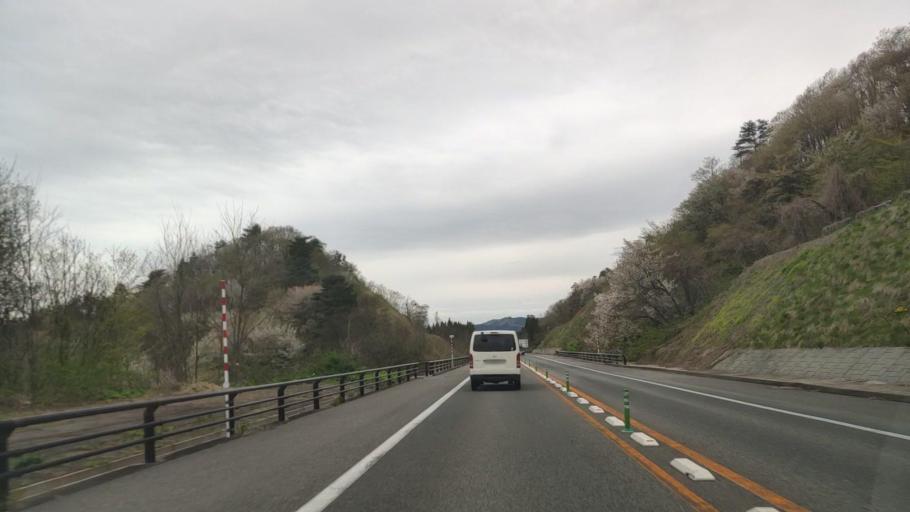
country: JP
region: Akita
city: Odate
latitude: 40.3200
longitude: 140.5920
